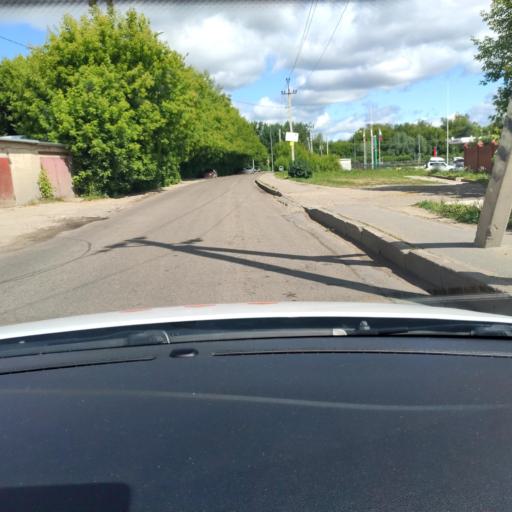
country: RU
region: Tatarstan
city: Vysokaya Gora
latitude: 55.8660
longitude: 49.2355
